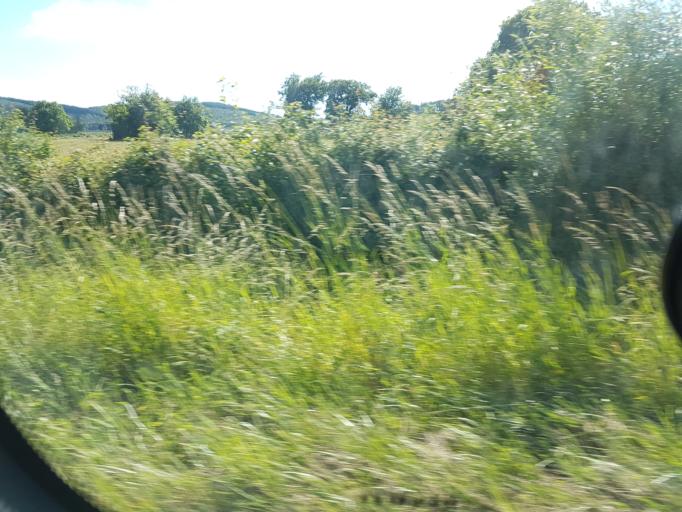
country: FR
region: Bourgogne
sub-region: Departement de Saone-et-Loire
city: Epinac
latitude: 46.9935
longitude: 4.4817
